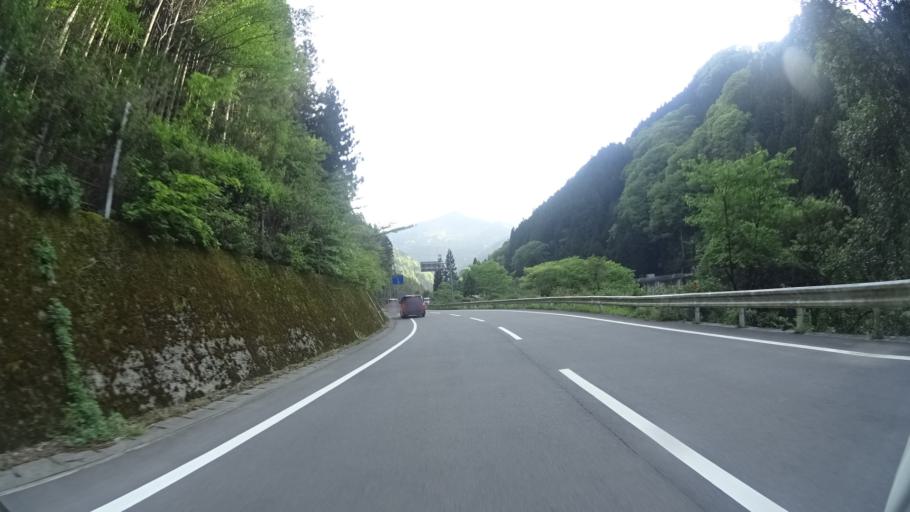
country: JP
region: Tokushima
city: Ikedacho
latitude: 33.8645
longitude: 133.9024
